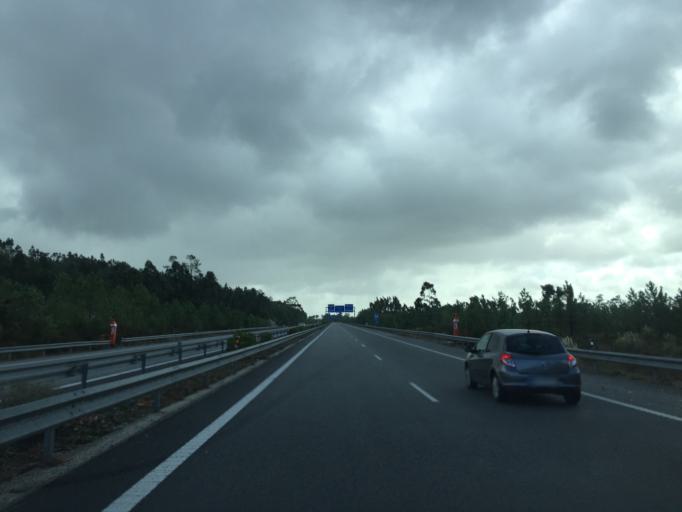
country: PT
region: Aveiro
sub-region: Mealhada
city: Pampilhosa do Botao
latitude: 40.2805
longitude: -8.5103
